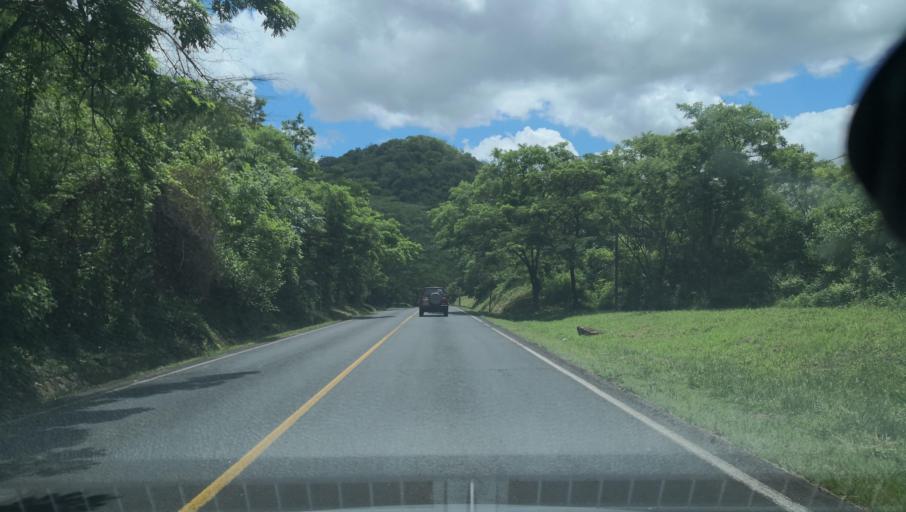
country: NI
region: Esteli
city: Condega
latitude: 13.3080
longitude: -86.3517
